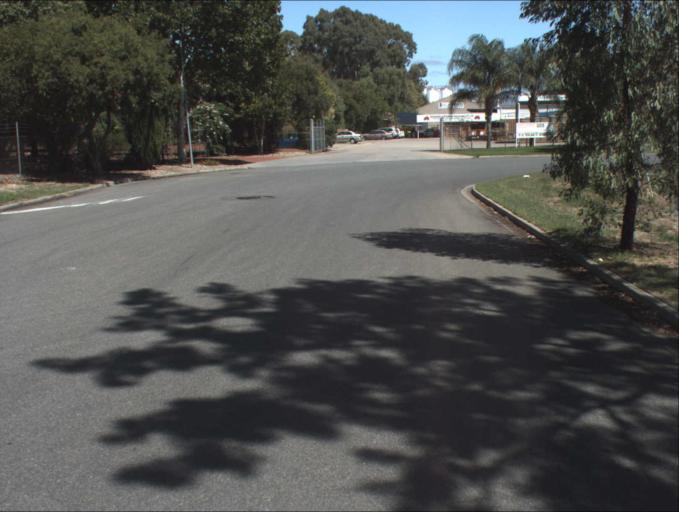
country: AU
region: South Australia
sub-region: Prospect
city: Prospect
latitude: -34.8695
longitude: 138.5736
